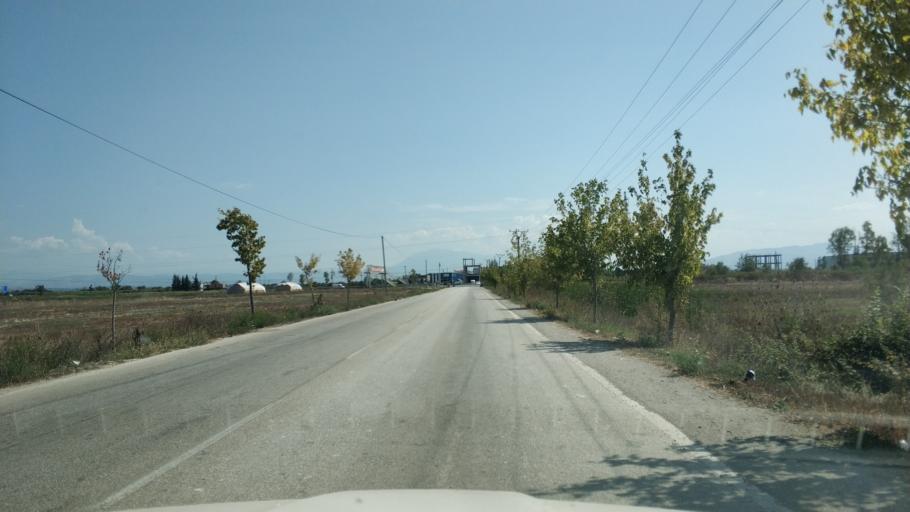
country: AL
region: Fier
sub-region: Rrethi i Lushnjes
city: Krutja e Poshtme
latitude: 40.8798
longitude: 19.6669
